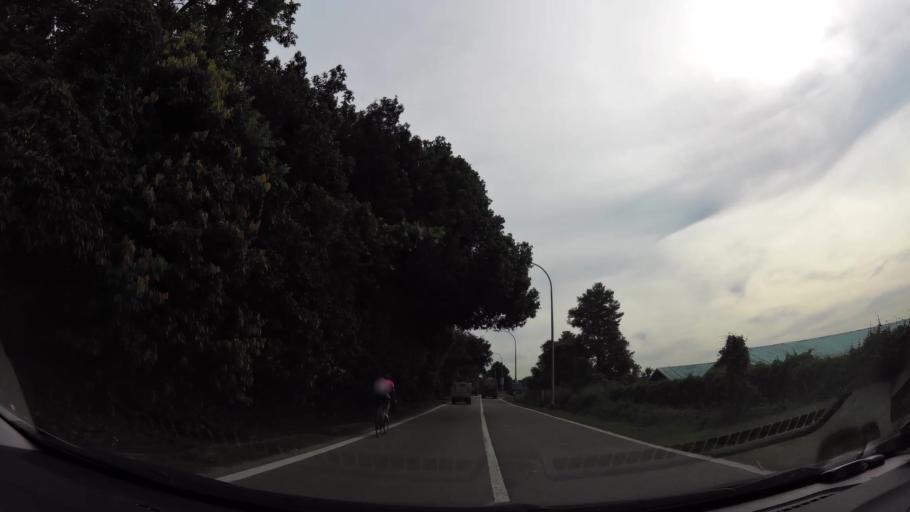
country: MY
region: Johor
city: Johor Bahru
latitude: 1.4335
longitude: 103.7249
